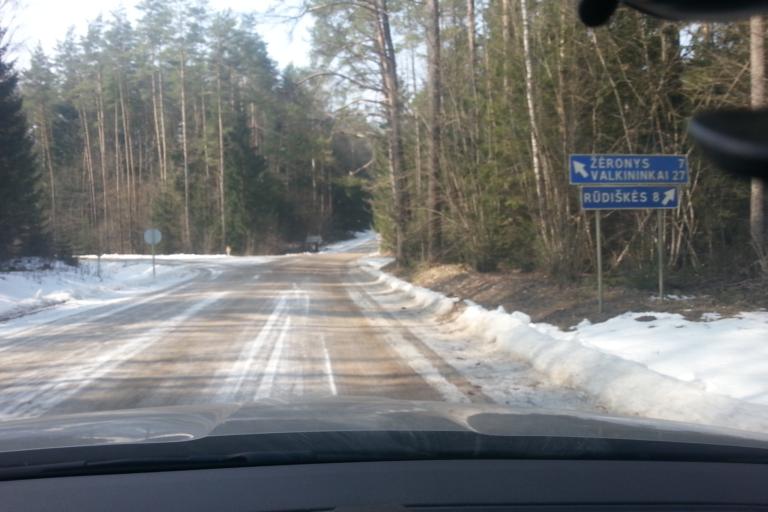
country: LT
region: Vilnius County
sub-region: Trakai
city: Rudiskes
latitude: 54.5107
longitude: 24.9310
